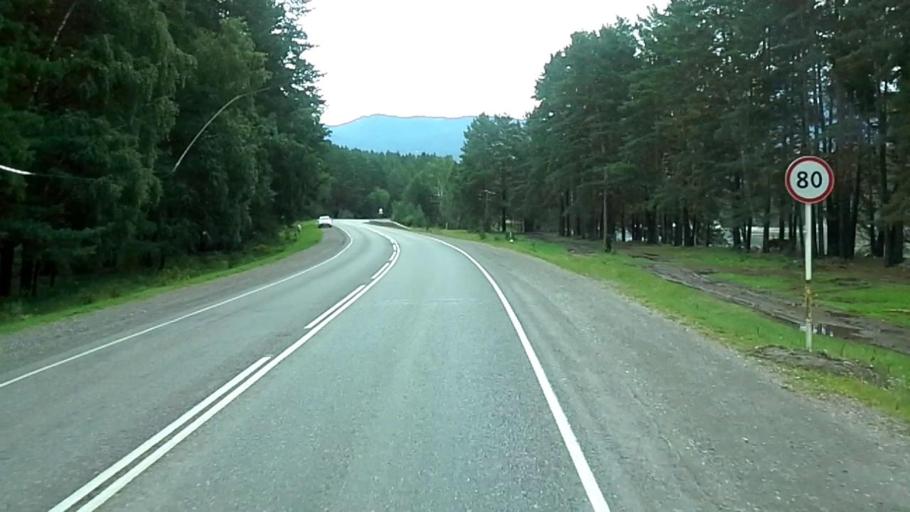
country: RU
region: Altay
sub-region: Mayminskiy Rayon
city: Manzherok
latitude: 51.8323
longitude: 85.7549
